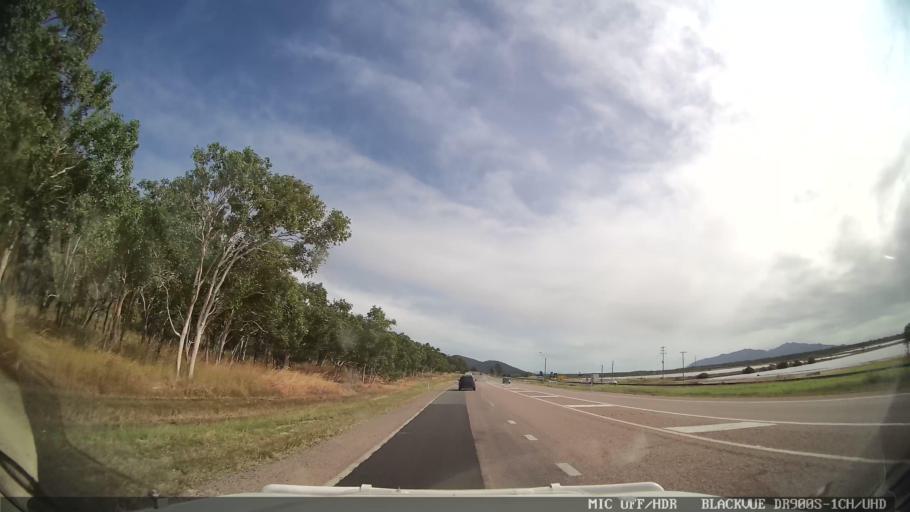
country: AU
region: Queensland
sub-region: Townsville
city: Townsville
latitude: -19.3976
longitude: 147.0226
